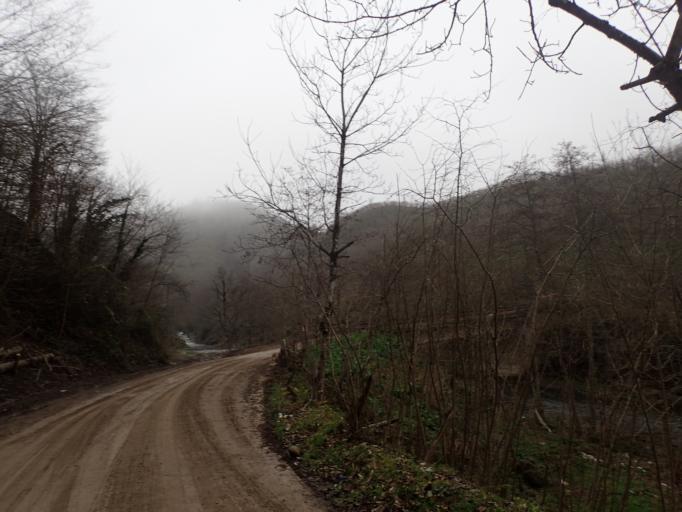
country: TR
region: Ordu
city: Camas
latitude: 40.9161
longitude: 37.5567
